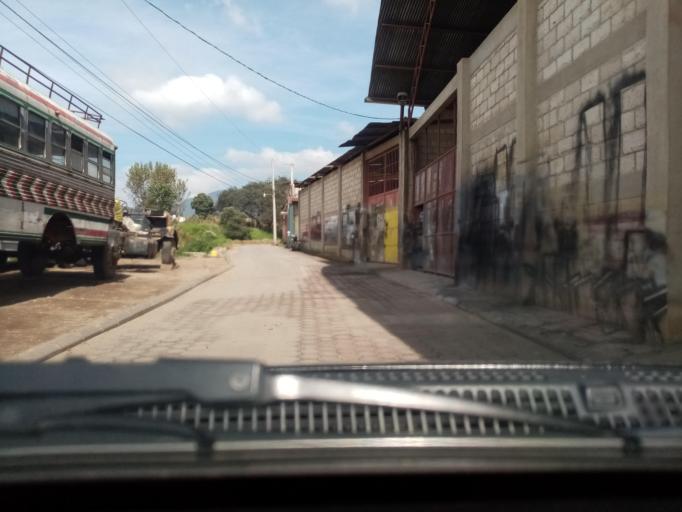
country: GT
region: Quetzaltenango
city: Quetzaltenango
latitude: 14.8570
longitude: -91.5297
